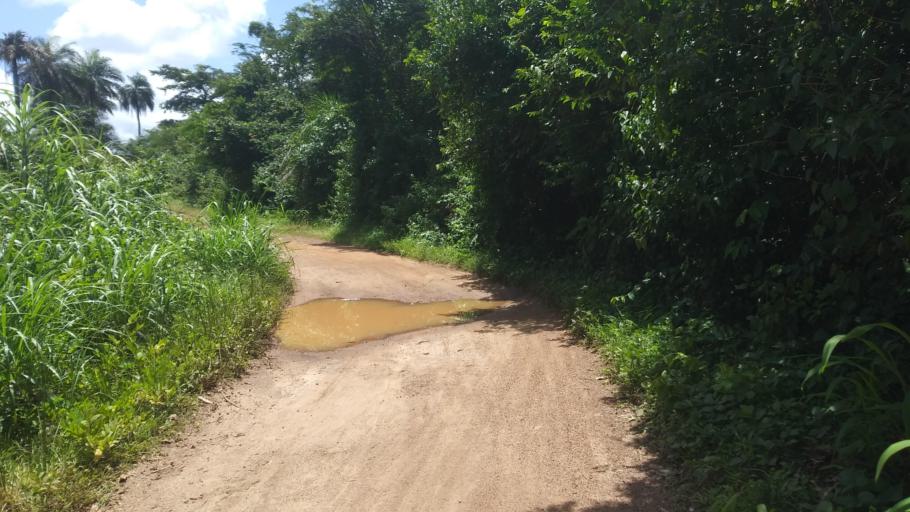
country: SL
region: Northern Province
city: Makeni
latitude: 8.8765
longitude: -11.9726
